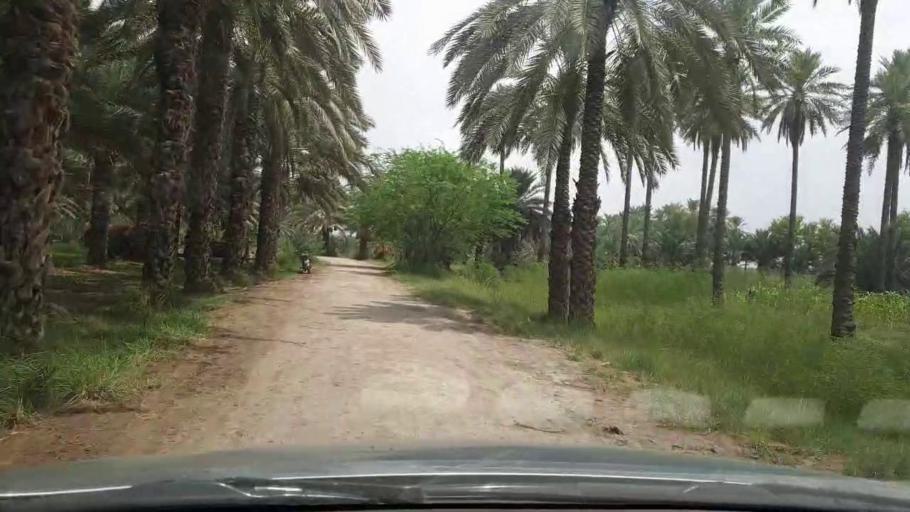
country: PK
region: Sindh
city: Kot Diji
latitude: 27.4284
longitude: 68.7571
